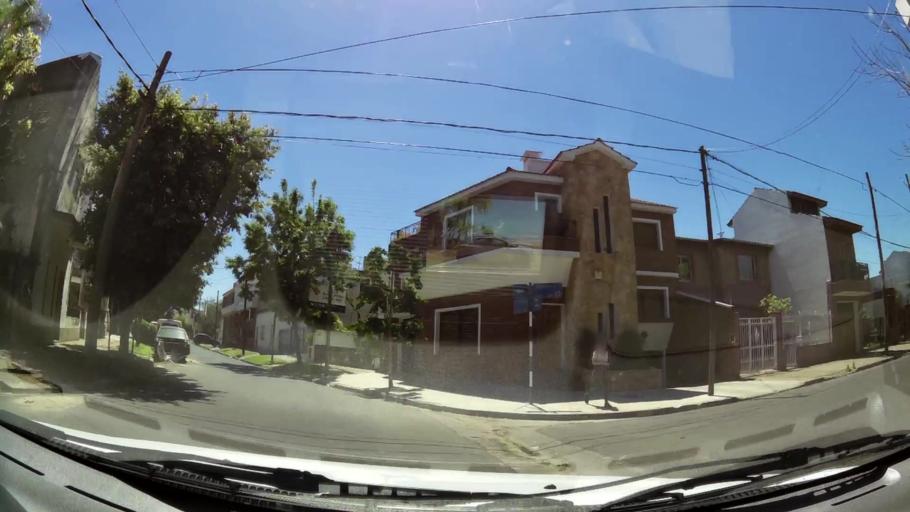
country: AR
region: Buenos Aires
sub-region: Partido de General San Martin
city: General San Martin
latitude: -34.5649
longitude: -58.5342
